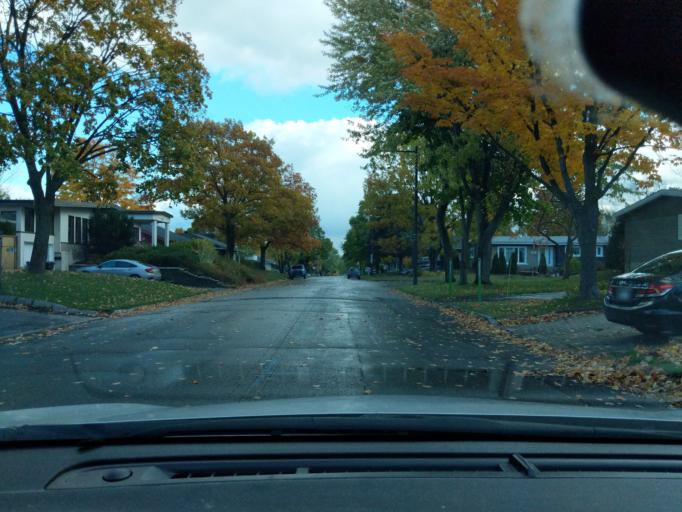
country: CA
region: Quebec
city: L'Ancienne-Lorette
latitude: 46.7641
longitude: -71.2894
